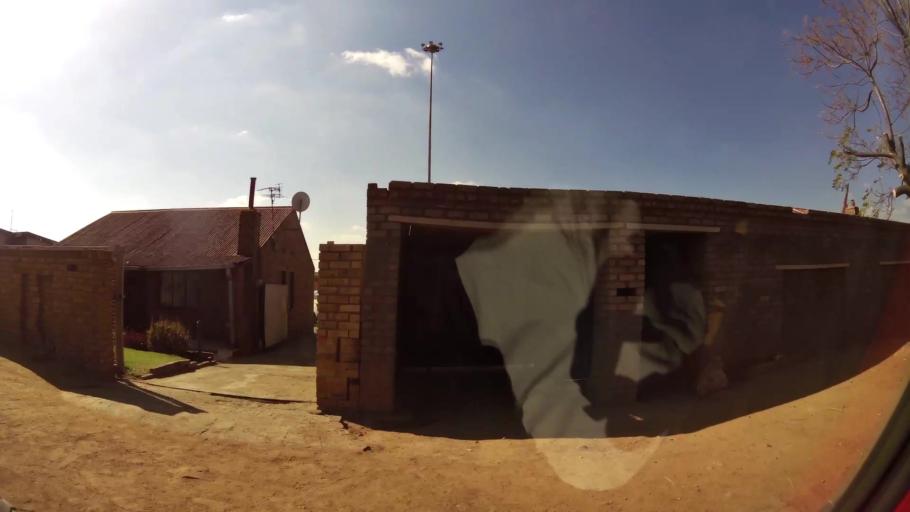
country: ZA
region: Gauteng
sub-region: City of Johannesburg Metropolitan Municipality
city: Soweto
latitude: -26.2332
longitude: 27.9102
